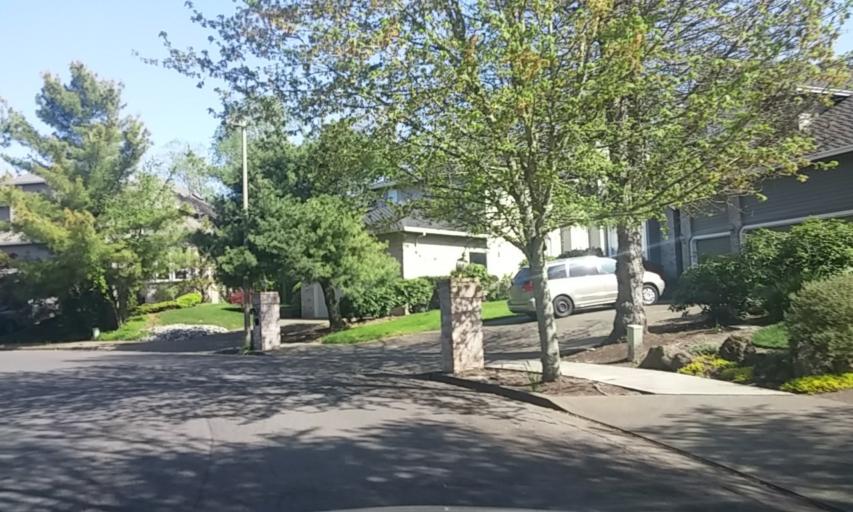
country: US
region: Oregon
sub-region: Washington County
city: Metzger
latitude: 45.4320
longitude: -122.7350
